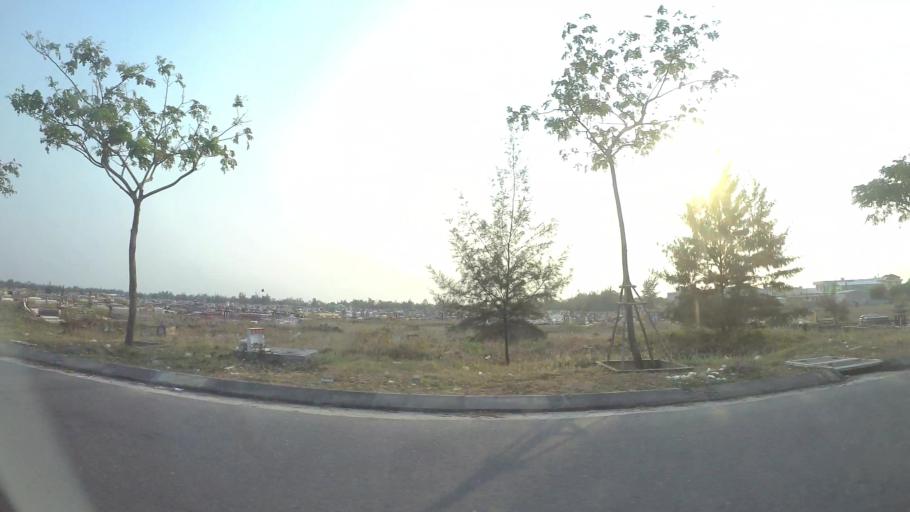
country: VN
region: Da Nang
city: Ngu Hanh Son
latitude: 15.9845
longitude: 108.2420
